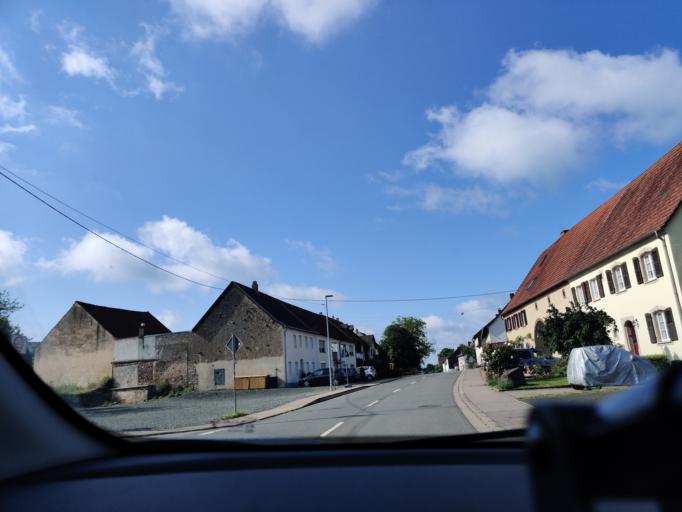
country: DE
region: Saarland
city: Gersheim
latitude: 49.1833
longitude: 7.1637
